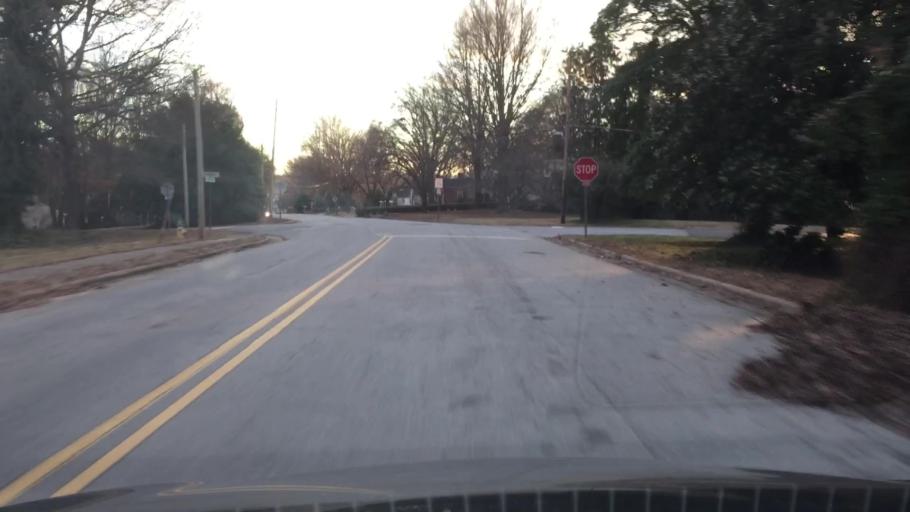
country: US
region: North Carolina
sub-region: Rockingham County
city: Reidsville
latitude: 36.3424
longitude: -79.6697
